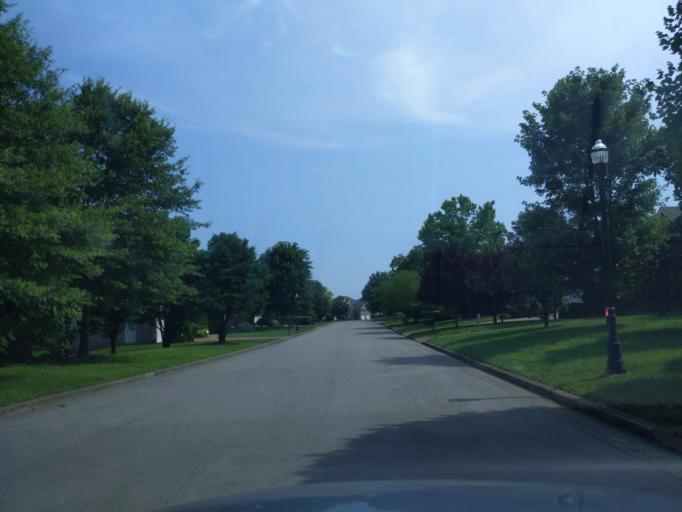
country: US
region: Tennessee
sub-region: Williamson County
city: Brentwood Estates
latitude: 36.0328
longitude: -86.7570
